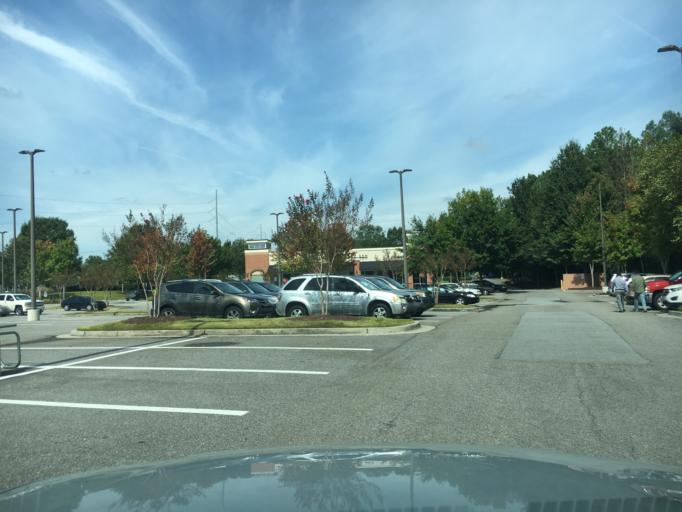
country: US
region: Georgia
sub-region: Fulton County
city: Johns Creek
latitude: 34.0138
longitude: -84.1835
